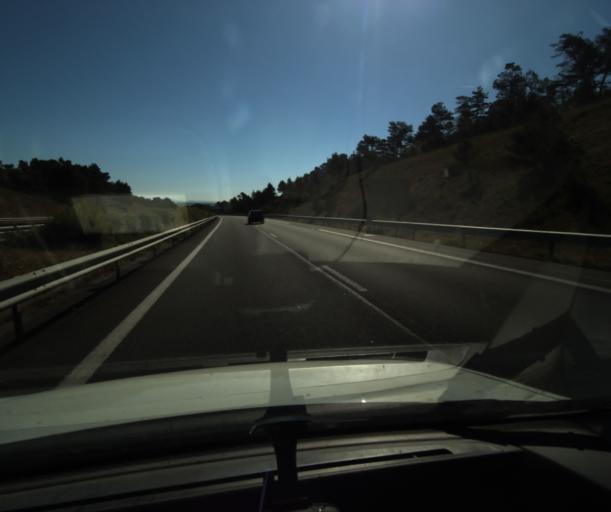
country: FR
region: Languedoc-Roussillon
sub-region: Departement de l'Aude
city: Palaja
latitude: 43.1865
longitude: 2.3989
